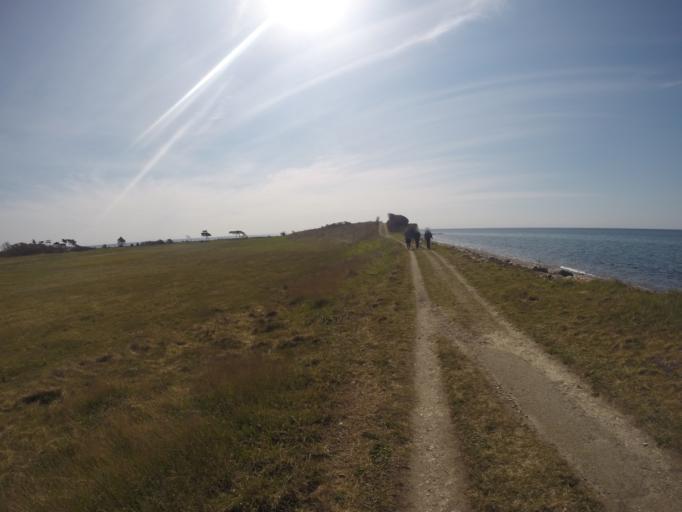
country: DK
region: Zealand
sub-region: Kalundborg Kommune
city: Gorlev
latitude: 55.5172
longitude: 11.0818
